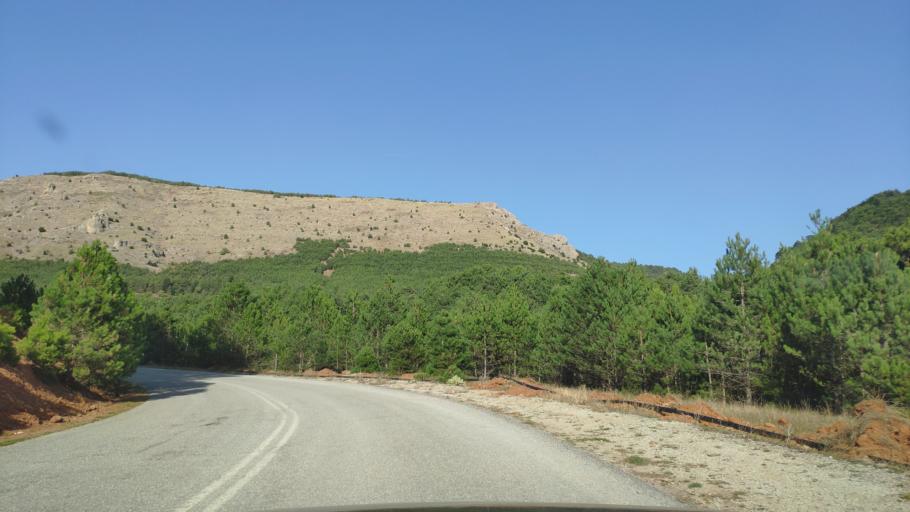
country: GR
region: West Greece
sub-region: Nomos Achaias
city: Aiyira
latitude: 38.0276
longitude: 22.4030
